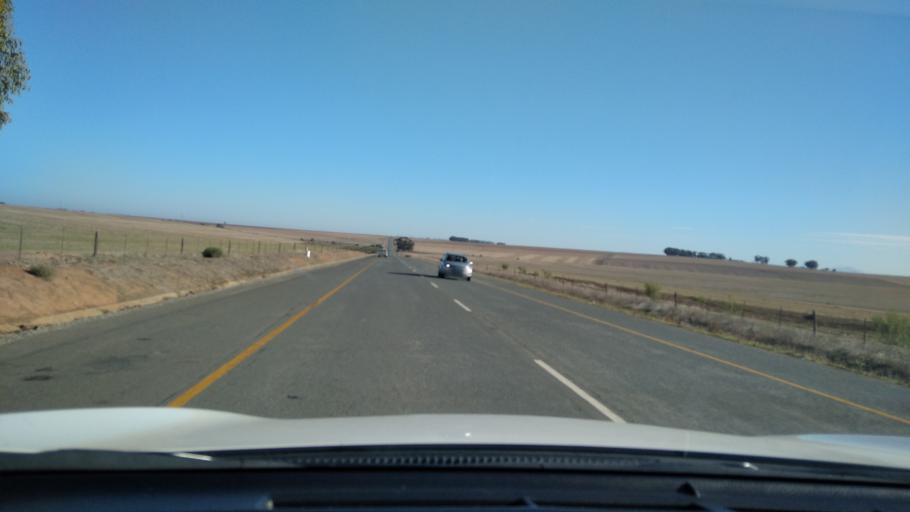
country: ZA
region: Western Cape
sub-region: West Coast District Municipality
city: Malmesbury
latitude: -33.3541
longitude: 18.6432
